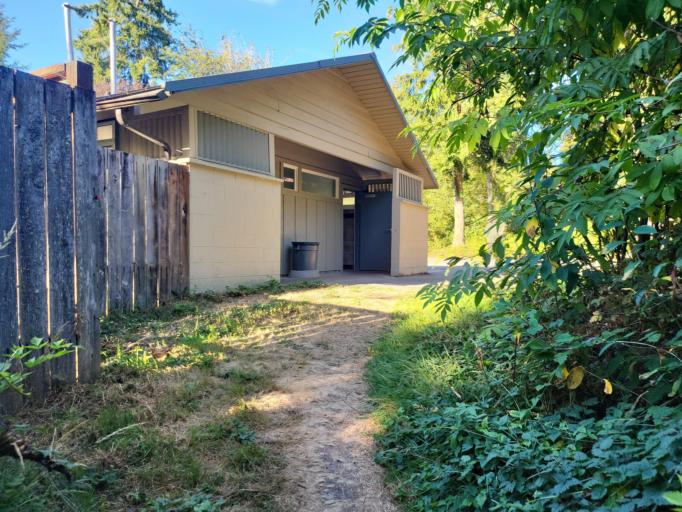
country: US
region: Washington
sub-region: Pierce County
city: Tacoma
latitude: 47.3156
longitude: -122.4057
